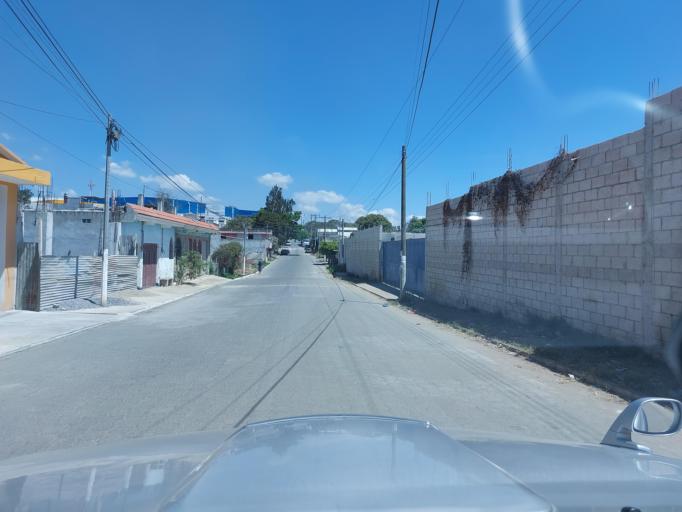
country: GT
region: Chimaltenango
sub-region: Municipio de Chimaltenango
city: Chimaltenango
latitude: 14.6565
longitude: -90.8294
